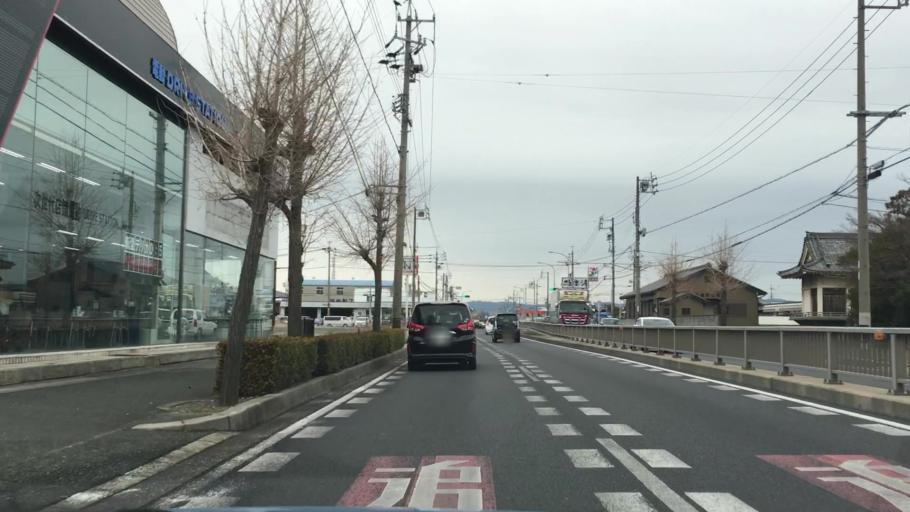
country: JP
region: Aichi
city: Toyohashi
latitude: 34.7866
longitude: 137.3770
